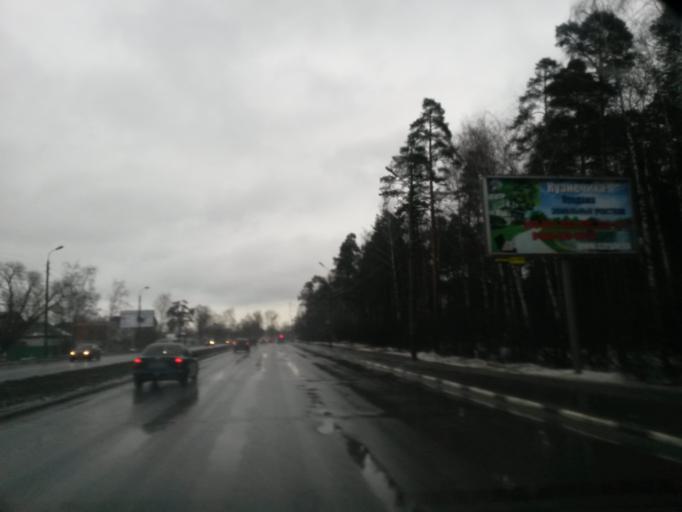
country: RU
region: Jaroslavl
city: Yaroslavl
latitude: 57.6501
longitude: 39.9296
